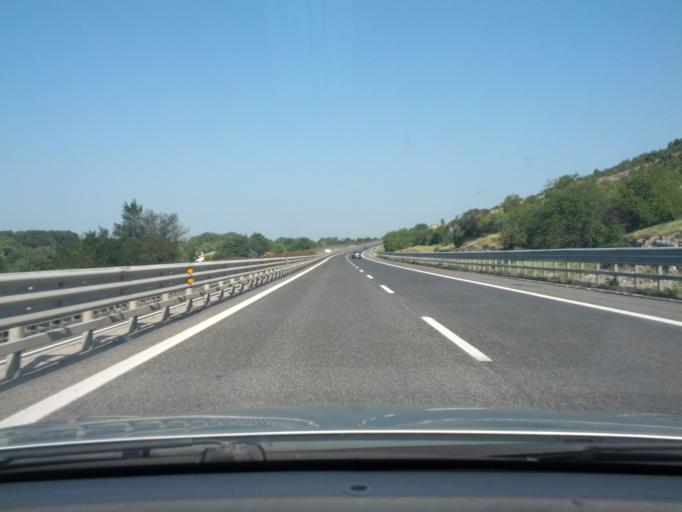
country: IT
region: Friuli Venezia Giulia
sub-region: Provincia di Gorizia
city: Monfalcone
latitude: 45.8189
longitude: 13.5361
